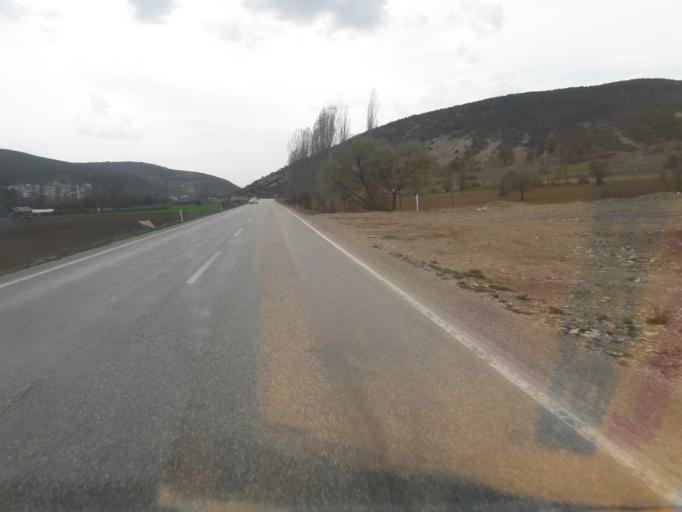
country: TR
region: Gumushane
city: Siran
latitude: 40.1771
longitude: 39.1458
